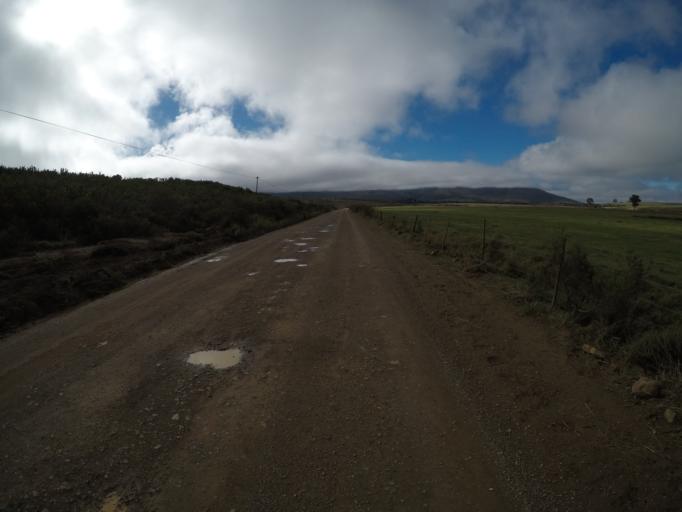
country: ZA
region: Western Cape
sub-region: Cape Winelands District Municipality
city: Ashton
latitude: -34.1258
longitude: 19.8239
